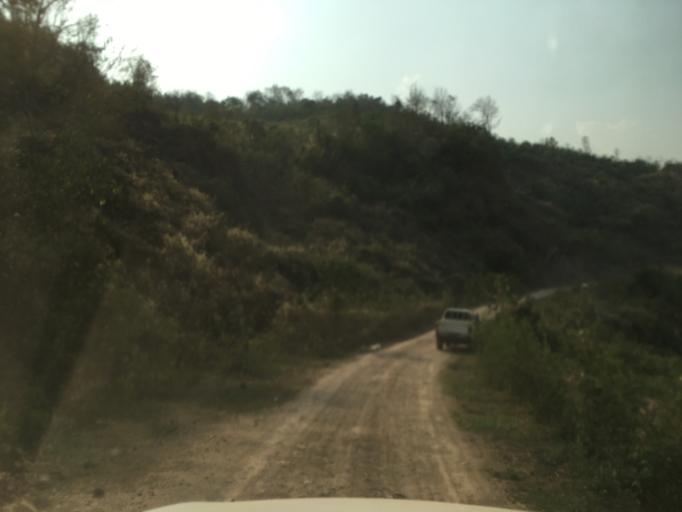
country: LA
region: Xiangkhoang
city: Phonsavan
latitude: 19.8195
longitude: 102.9953
